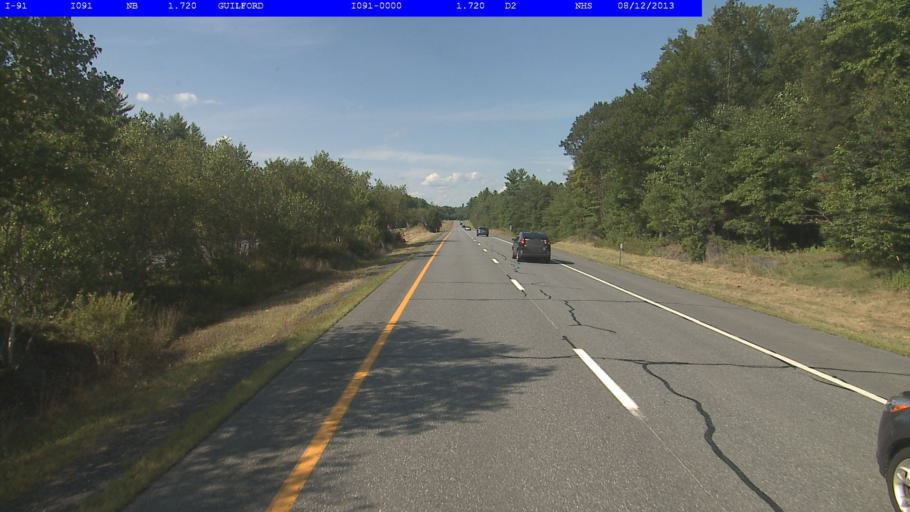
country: US
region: Massachusetts
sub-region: Franklin County
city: Bernardston
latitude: 42.7548
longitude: -72.5661
